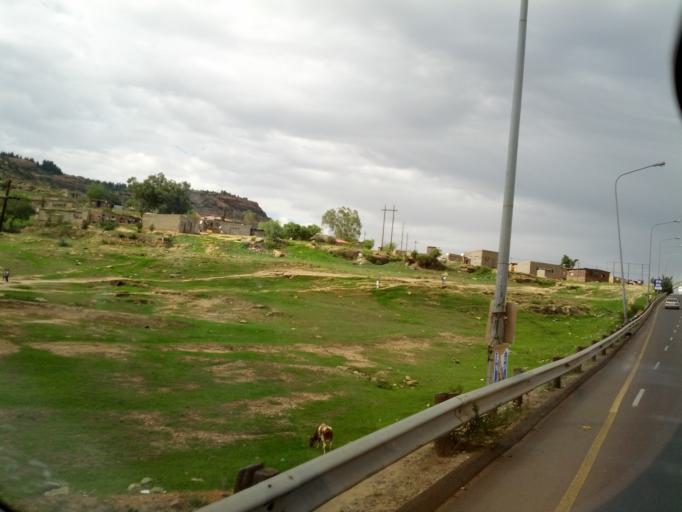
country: LS
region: Maseru
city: Maseru
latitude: -29.3364
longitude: 27.4733
